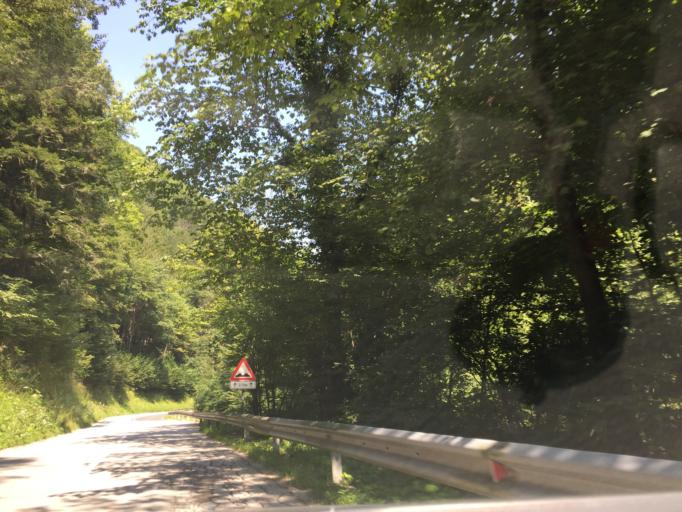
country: SI
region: Prebold
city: Prebold
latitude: 46.2113
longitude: 15.0915
